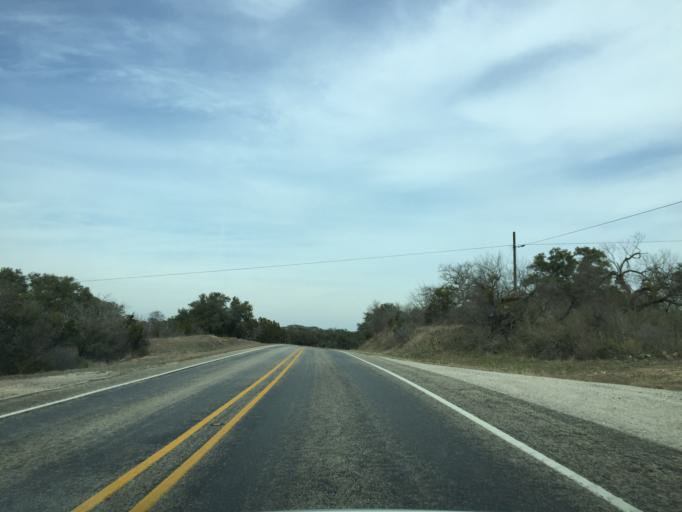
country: US
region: Texas
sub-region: Gillespie County
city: Fredericksburg
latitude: 30.4756
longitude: -98.7092
